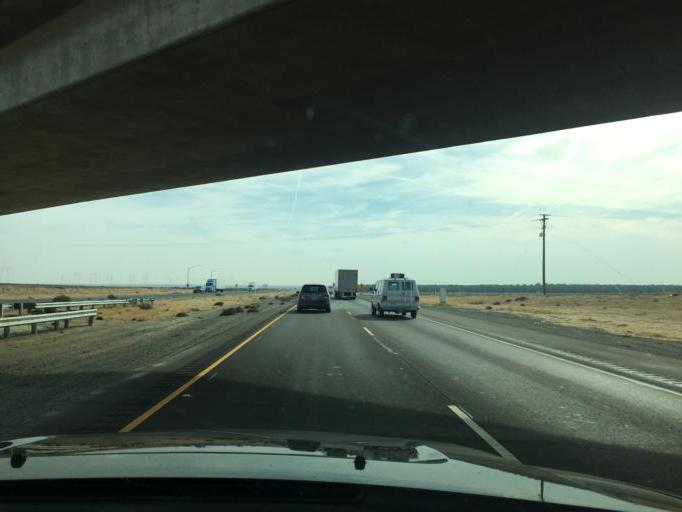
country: US
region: California
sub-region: Kings County
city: Kettleman City
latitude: 35.9349
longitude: -119.9126
